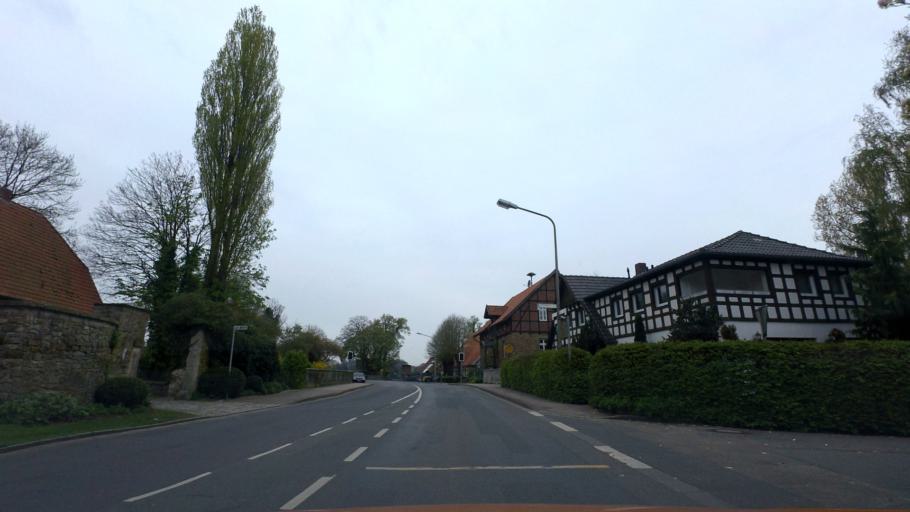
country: DE
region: Lower Saxony
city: Rieste
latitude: 52.4493
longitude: 8.0268
